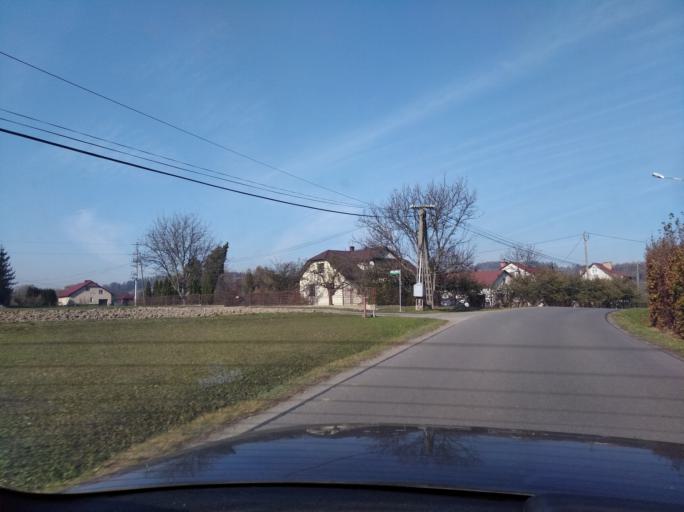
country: PL
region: Subcarpathian Voivodeship
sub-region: Powiat strzyzowski
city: Wisniowa
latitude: 49.8681
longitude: 21.6397
